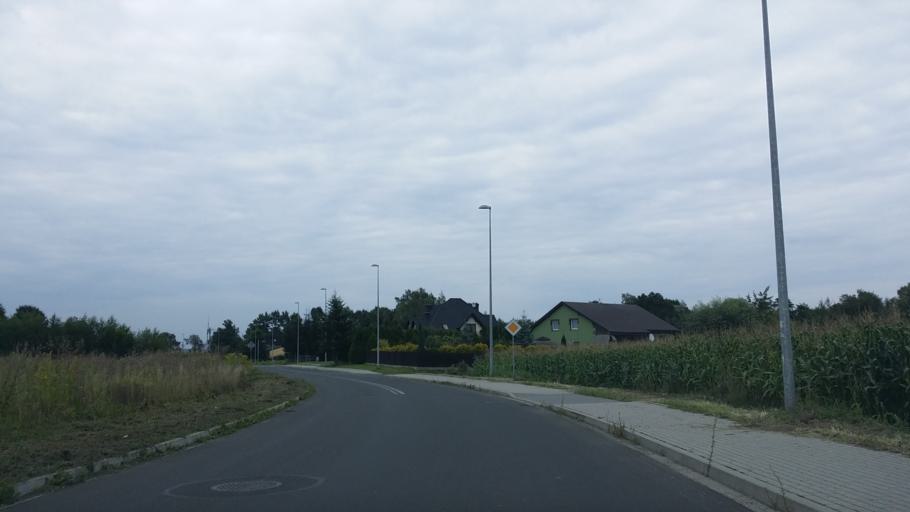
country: PL
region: Lesser Poland Voivodeship
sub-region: Powiat oswiecimski
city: Zator
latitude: 49.9943
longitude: 19.4263
